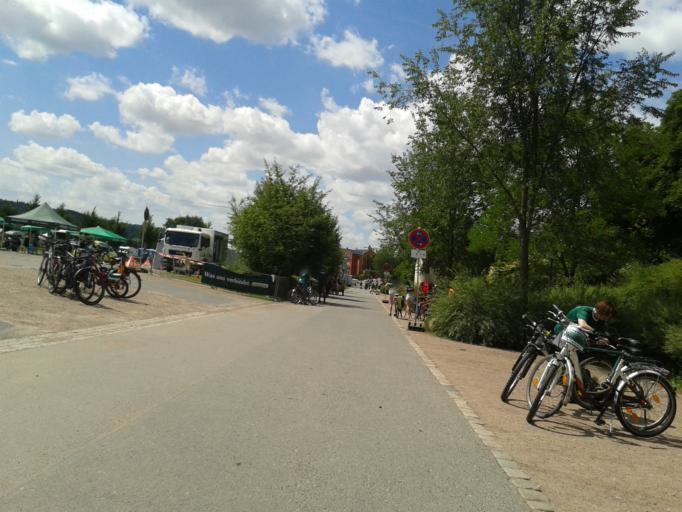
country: DE
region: Saxony
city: Radebeul
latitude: 51.1042
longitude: 13.6273
